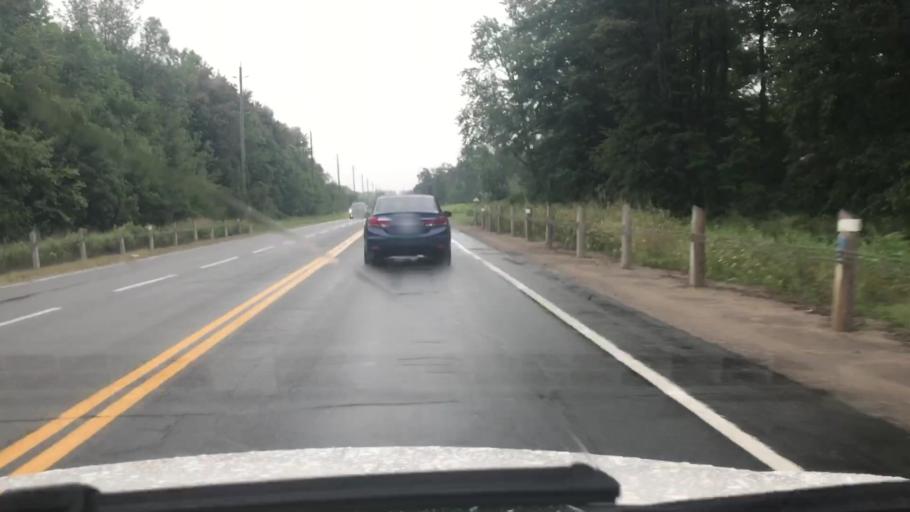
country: CA
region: Ontario
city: Bradford West Gwillimbury
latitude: 44.2021
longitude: -79.6463
